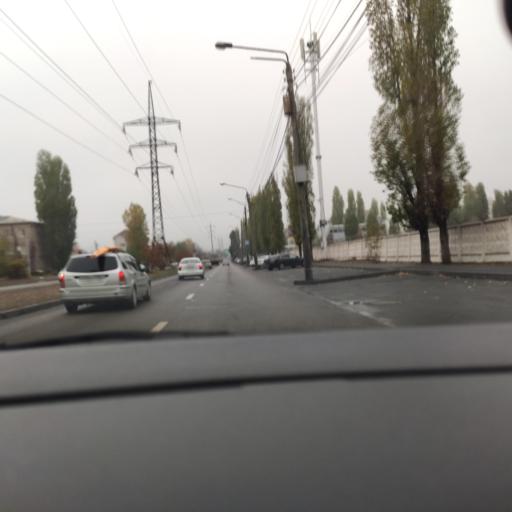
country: RU
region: Voronezj
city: Voronezh
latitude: 51.6333
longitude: 39.1797
